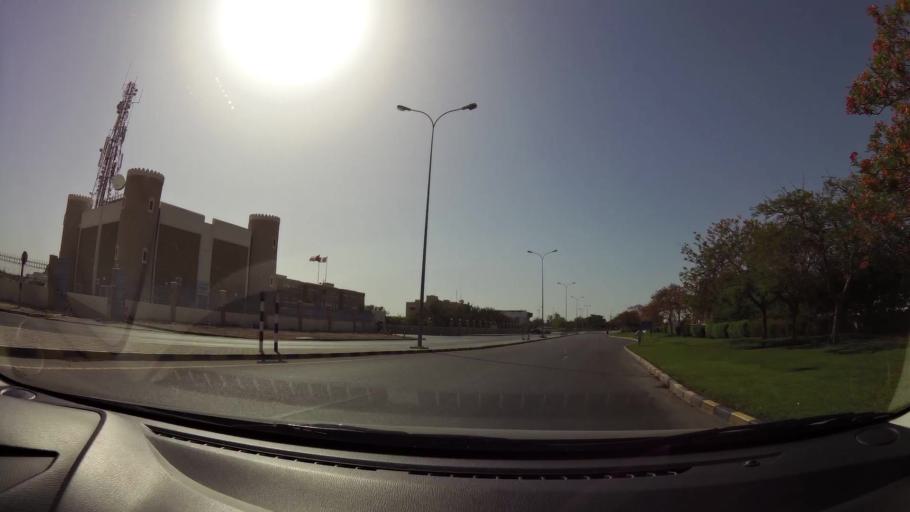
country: OM
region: Muhafazat Masqat
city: Bawshar
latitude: 23.5829
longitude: 58.2920
